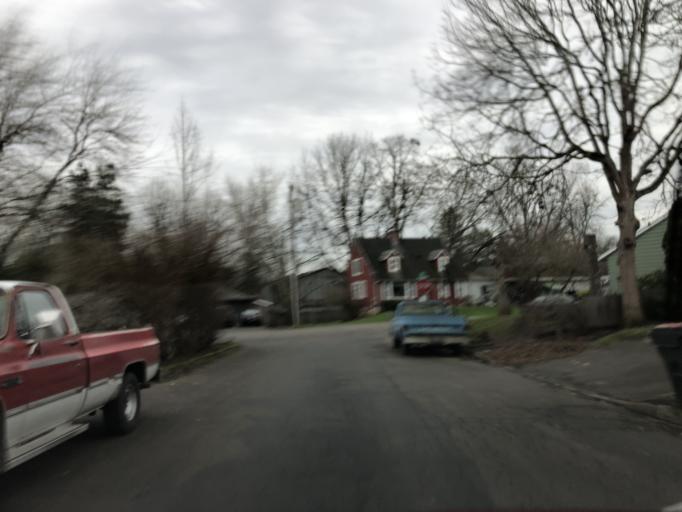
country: US
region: Oregon
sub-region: Washington County
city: Tigard
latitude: 45.4327
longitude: -122.7709
